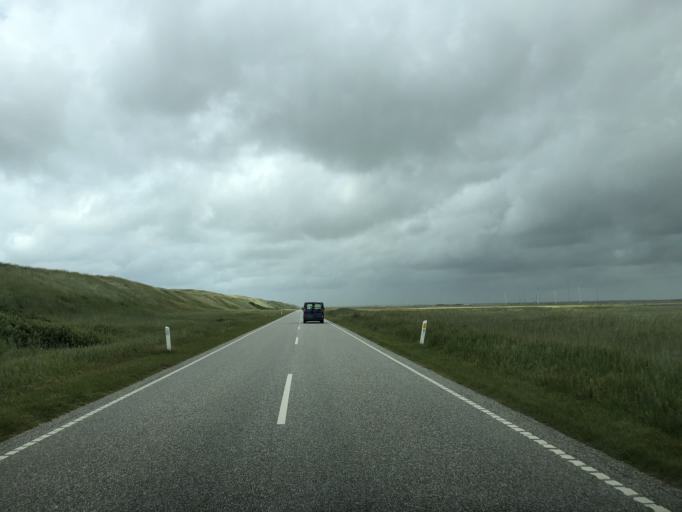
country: DK
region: Central Jutland
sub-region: Lemvig Kommune
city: Harboore
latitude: 56.4142
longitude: 8.1229
